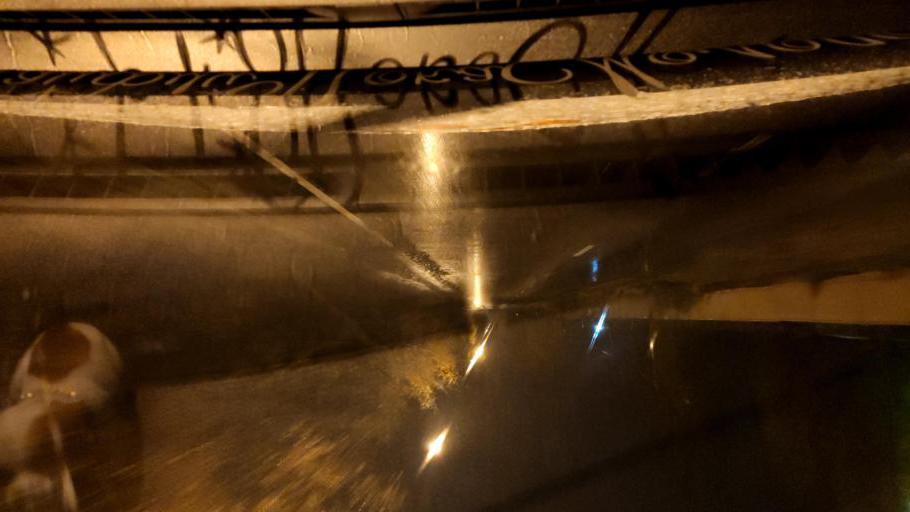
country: RU
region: Voronezj
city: Somovo
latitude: 51.7219
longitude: 39.2952
